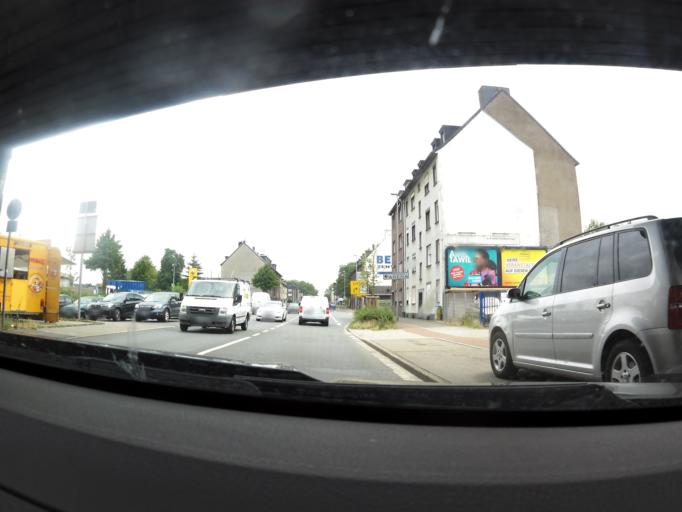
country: DE
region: North Rhine-Westphalia
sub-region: Regierungsbezirk Dusseldorf
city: Oberhausen
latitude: 51.4812
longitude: 6.8445
